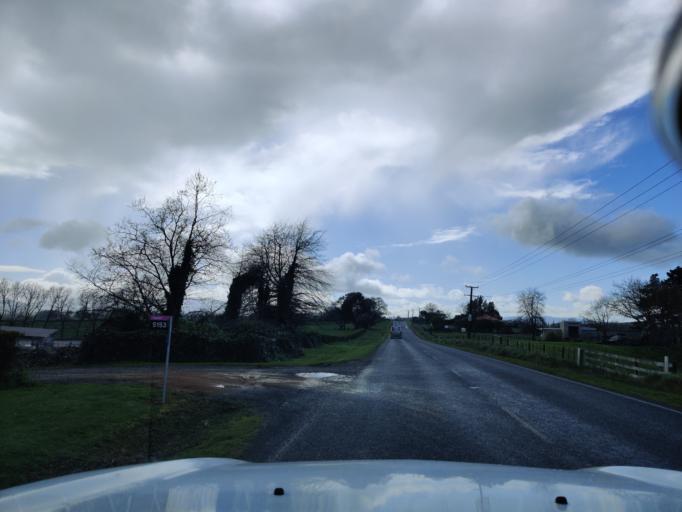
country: NZ
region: Waikato
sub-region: Waikato District
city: Ngaruawahia
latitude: -37.5735
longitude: 175.2447
